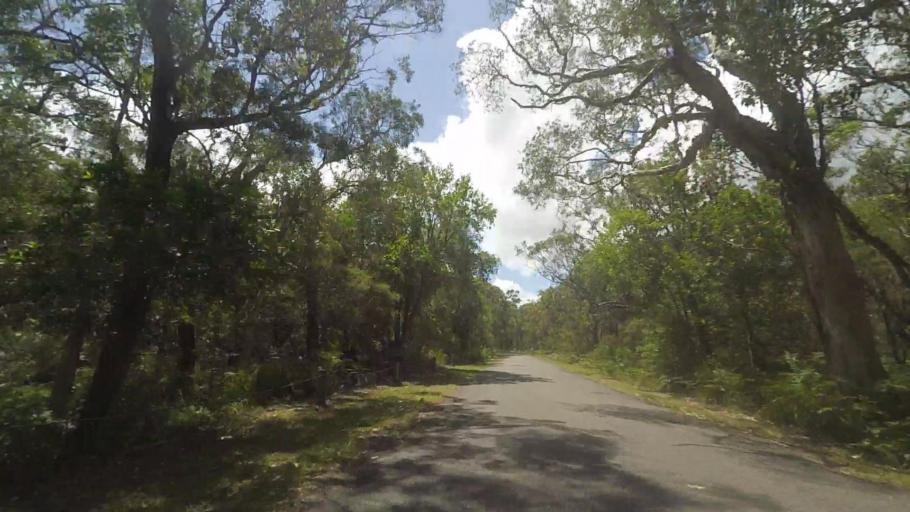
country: AU
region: New South Wales
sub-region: Great Lakes
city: Bulahdelah
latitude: -32.5087
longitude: 152.3178
